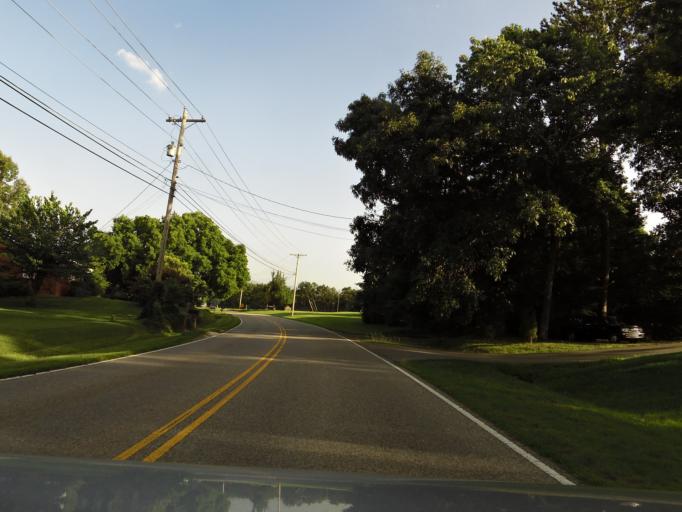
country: US
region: Tennessee
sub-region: Blount County
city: Eagleton Village
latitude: 35.8004
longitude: -83.9071
